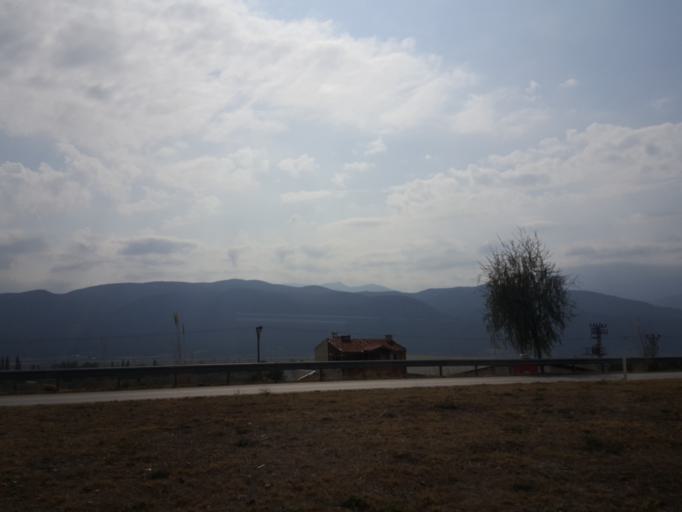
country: TR
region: Corum
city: Kargi
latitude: 41.1365
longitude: 34.4660
